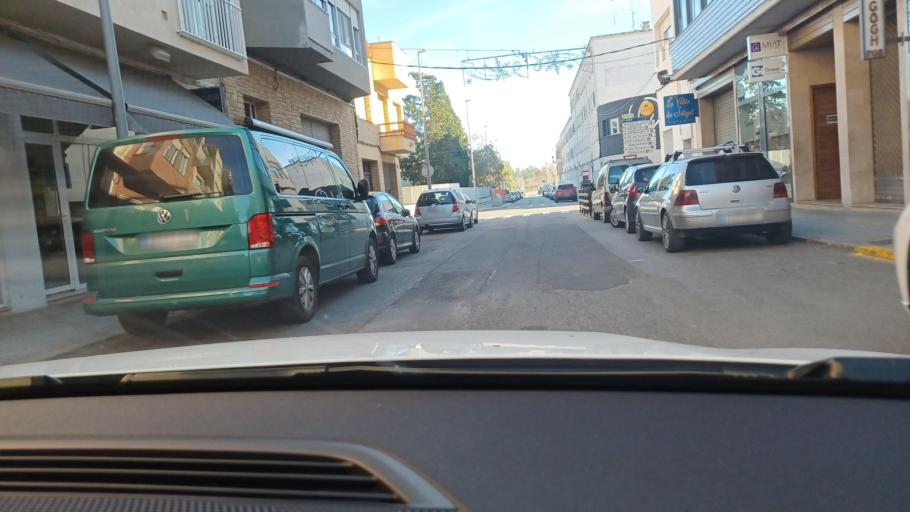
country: ES
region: Catalonia
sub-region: Provincia de Tarragona
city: Amposta
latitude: 40.7098
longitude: 0.5805
